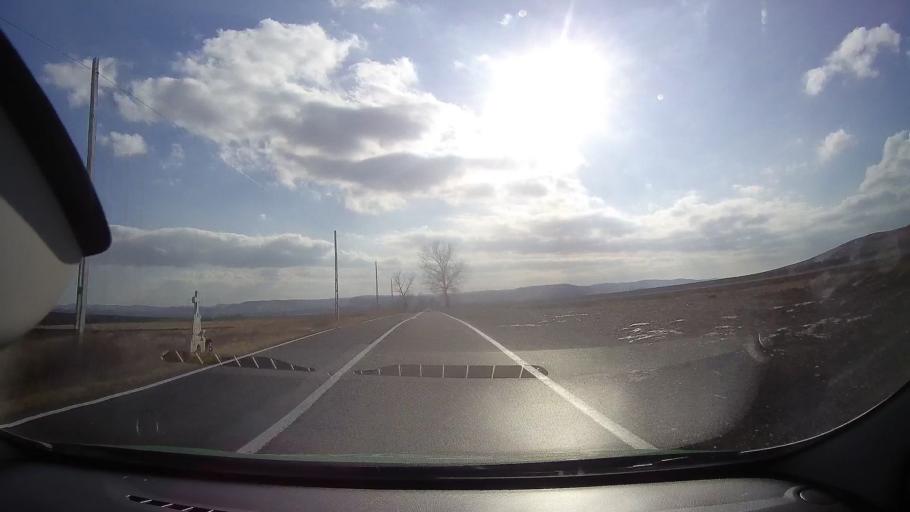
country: RO
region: Tulcea
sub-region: Comuna Nalbant
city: Nicolae Balcescu
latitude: 45.0143
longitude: 28.5998
